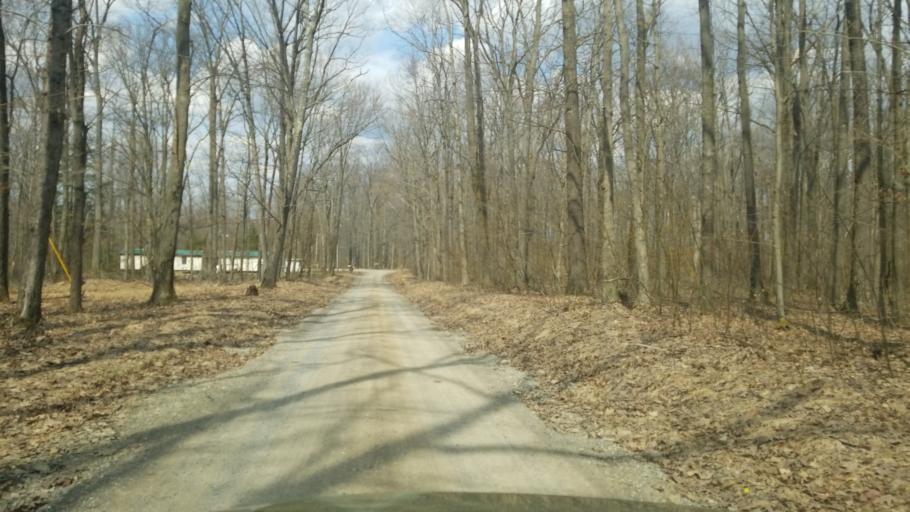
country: US
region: Pennsylvania
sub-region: Clearfield County
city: Clearfield
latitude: 41.1671
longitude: -78.5032
